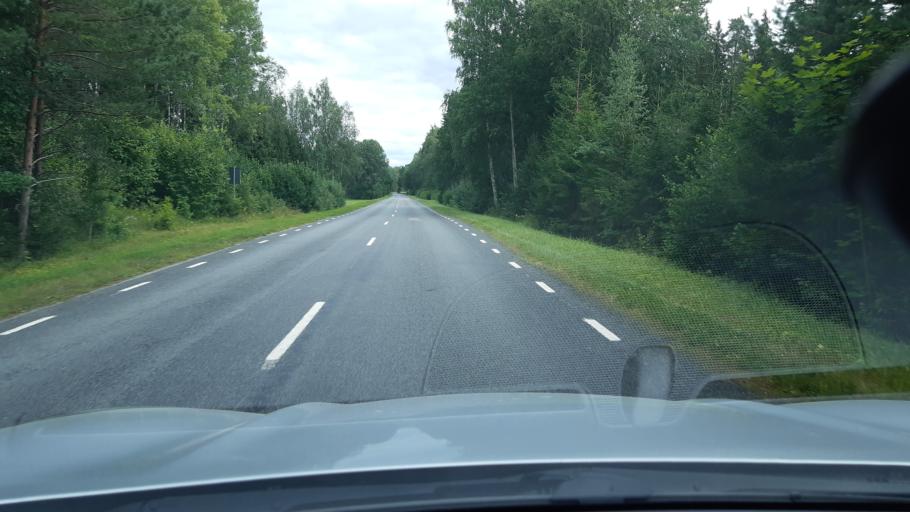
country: EE
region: Raplamaa
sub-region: Maerjamaa vald
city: Marjamaa
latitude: 59.0420
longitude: 24.5391
